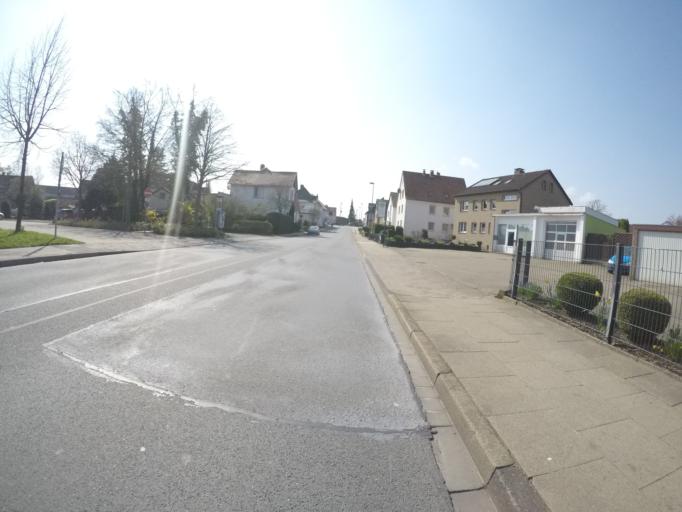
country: DE
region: North Rhine-Westphalia
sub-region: Regierungsbezirk Detmold
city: Herford
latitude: 52.0718
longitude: 8.6062
